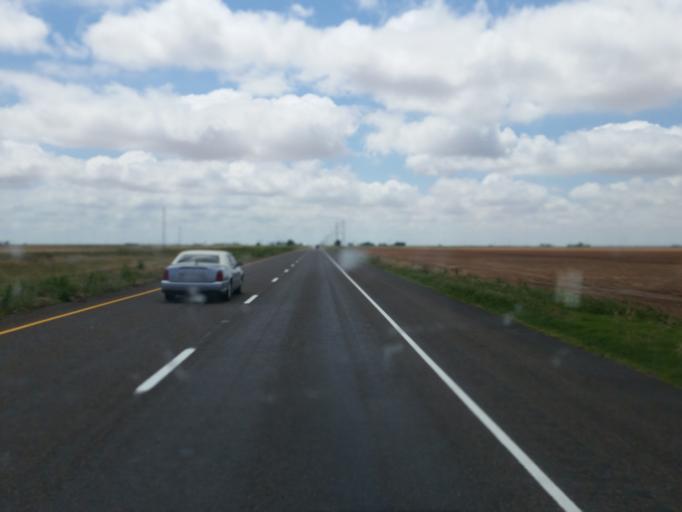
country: US
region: Texas
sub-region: Lubbock County
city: Slaton
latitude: 33.4110
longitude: -101.6281
